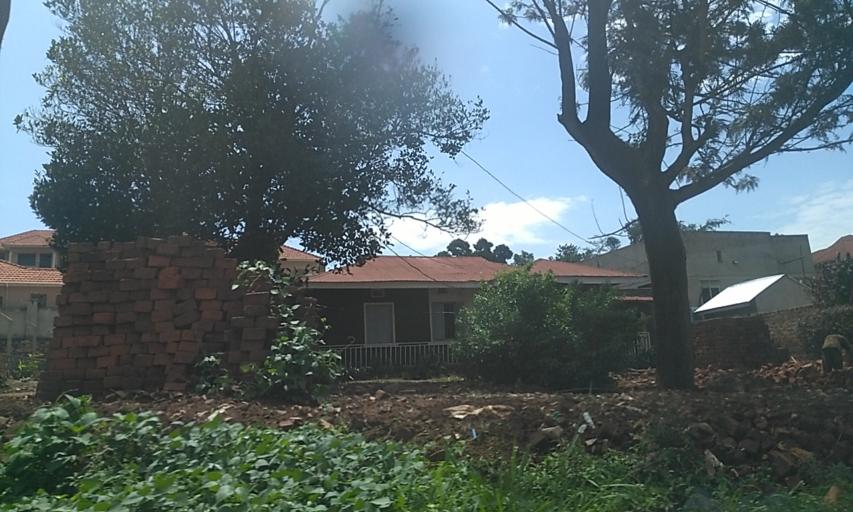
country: UG
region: Central Region
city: Kampala Central Division
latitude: 0.3841
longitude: 32.5941
